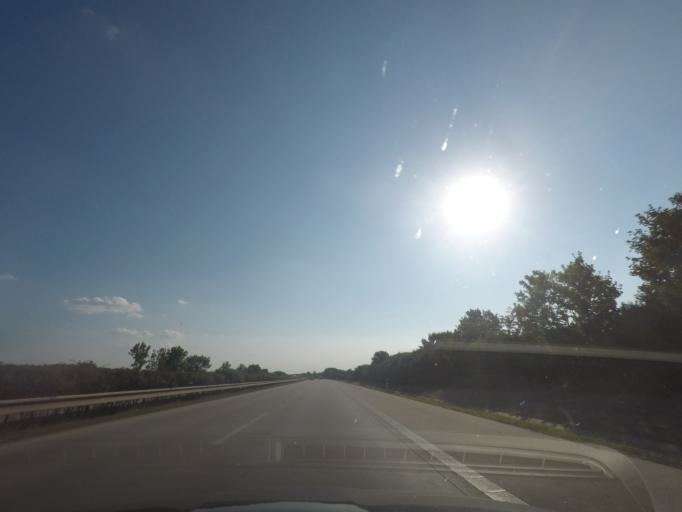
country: CZ
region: Olomoucky
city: Velky Tynec
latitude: 49.5712
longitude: 17.3460
